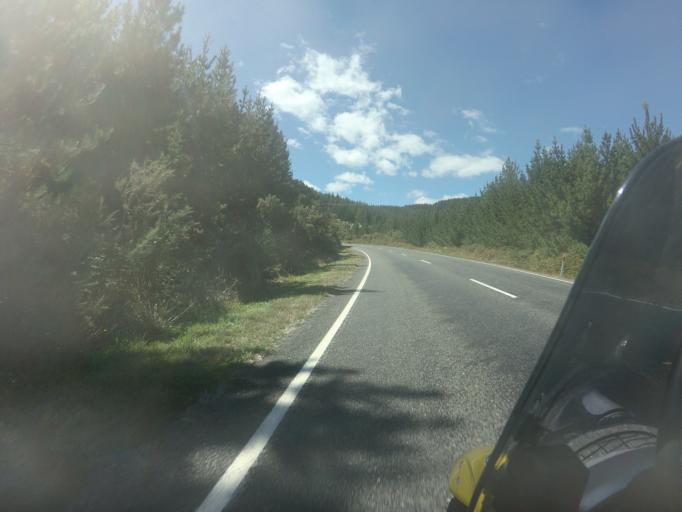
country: NZ
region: Bay of Plenty
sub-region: Whakatane District
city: Murupara
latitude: -38.2847
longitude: 176.8143
